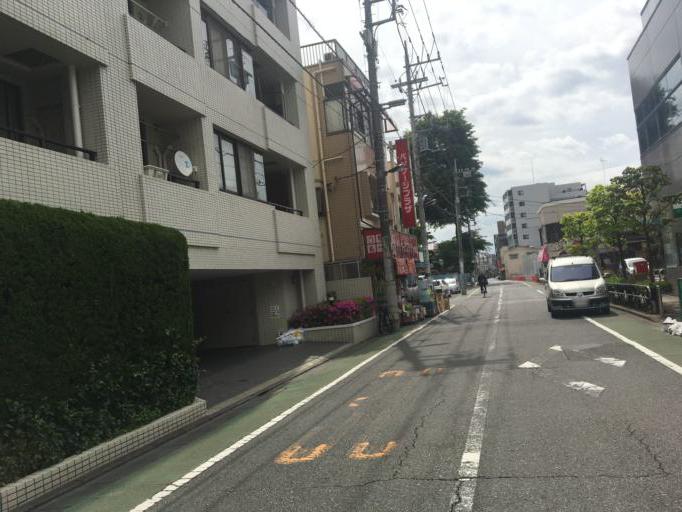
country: JP
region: Saitama
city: Shimotoda
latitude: 35.7642
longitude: 139.6706
